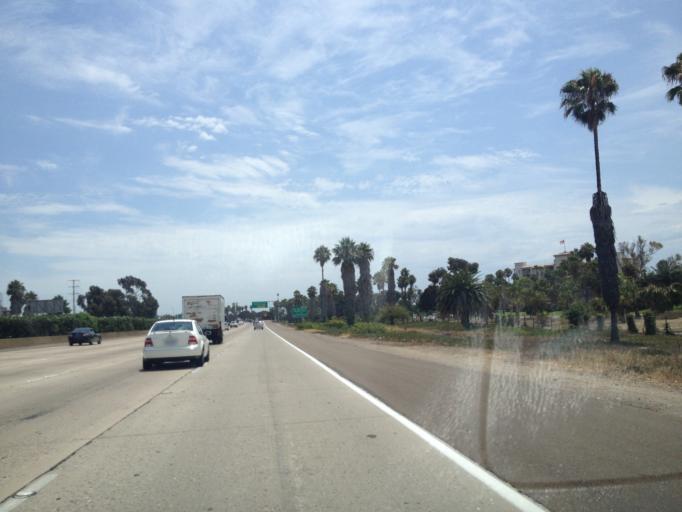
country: US
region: California
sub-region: San Diego County
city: San Diego
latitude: 32.7819
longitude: -117.2084
